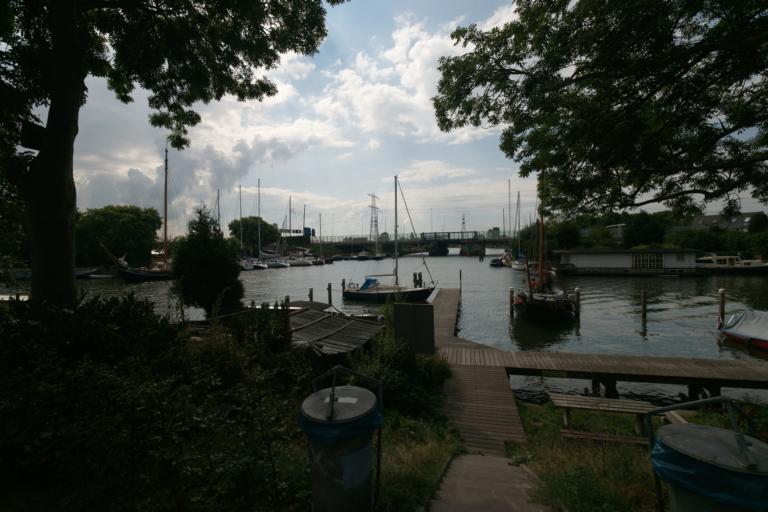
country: NL
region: North Holland
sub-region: Gemeente Weesp
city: Weesp
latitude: 52.3279
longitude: 5.0659
